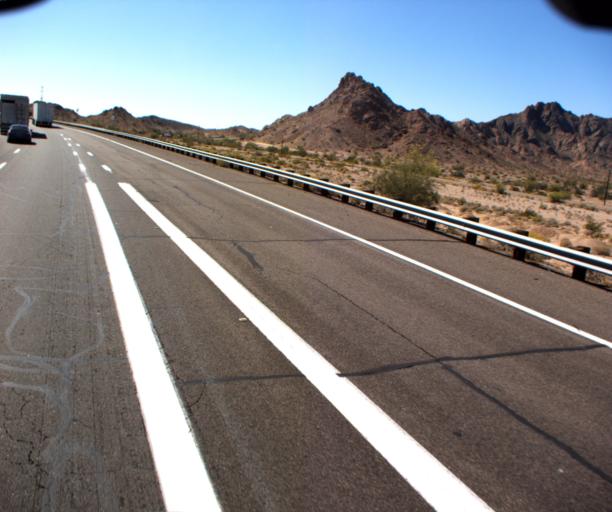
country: US
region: Arizona
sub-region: Yuma County
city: Wellton
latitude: 32.7294
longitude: -113.7338
